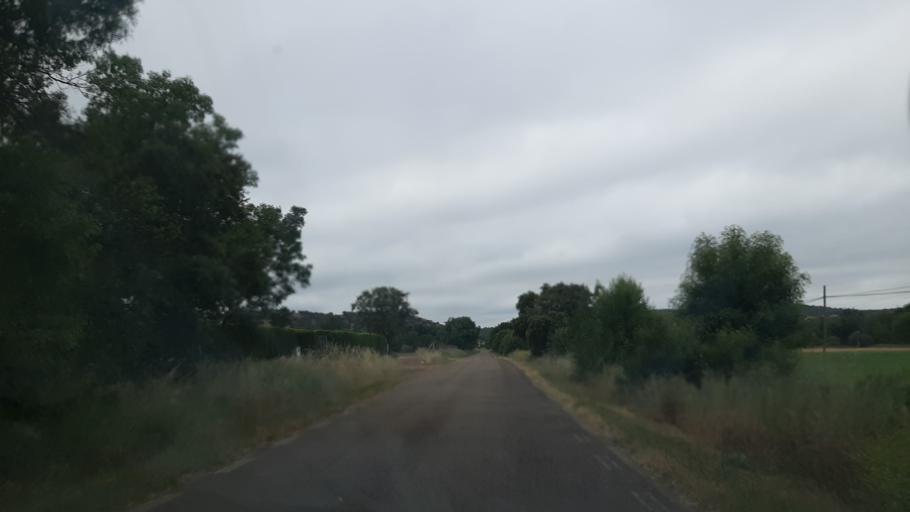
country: ES
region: Castille and Leon
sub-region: Provincia de Salamanca
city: Pastores
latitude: 40.5614
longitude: -6.4859
